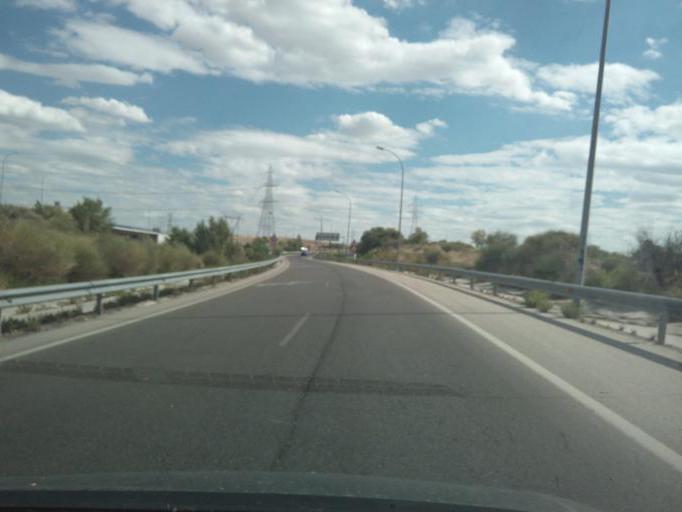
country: ES
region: Madrid
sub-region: Provincia de Madrid
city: San Sebastian de los Reyes
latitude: 40.5544
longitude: -3.6084
